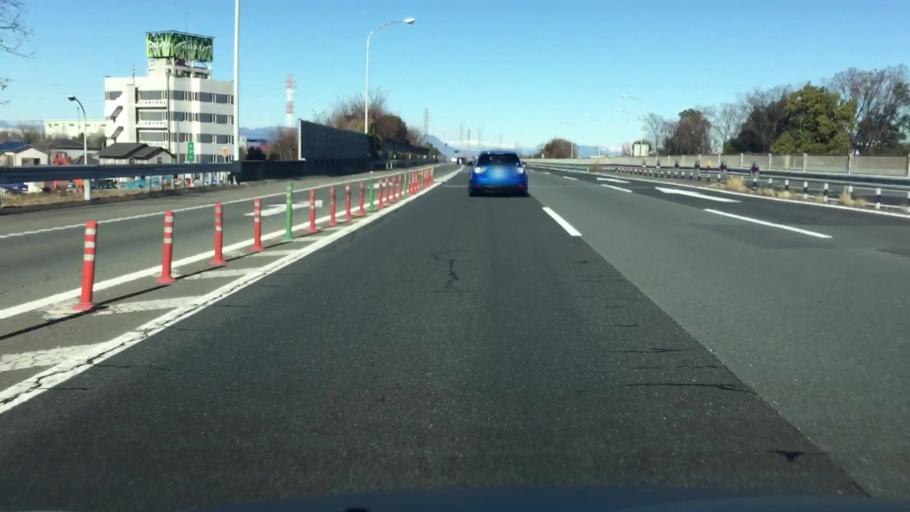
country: JP
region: Saitama
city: Honjo
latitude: 36.2187
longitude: 139.1643
